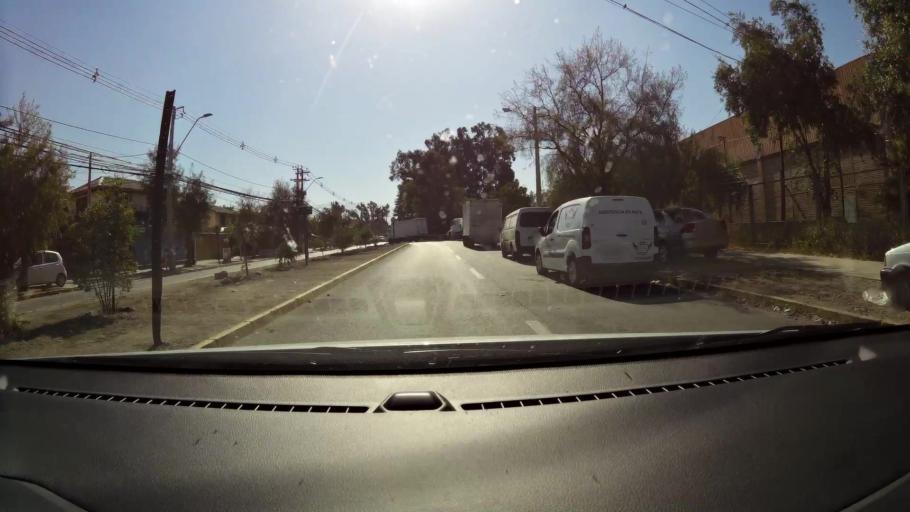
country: CL
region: Santiago Metropolitan
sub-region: Provincia de Maipo
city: San Bernardo
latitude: -33.5670
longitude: -70.7064
